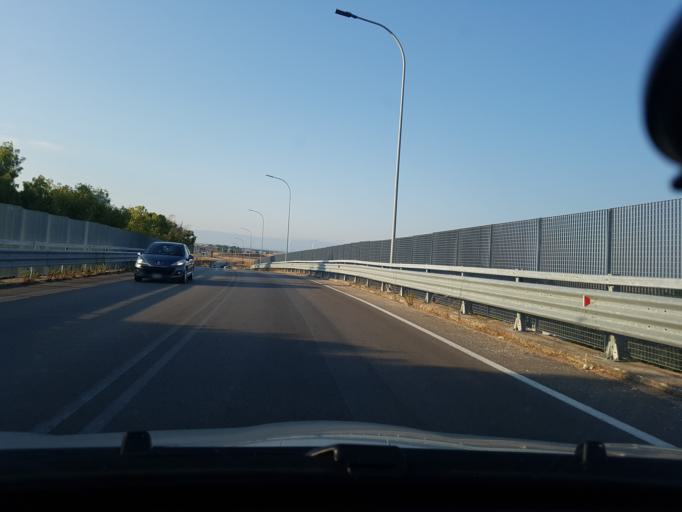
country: IT
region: Apulia
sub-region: Provincia di Foggia
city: Carapelle
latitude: 41.4069
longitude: 15.6531
